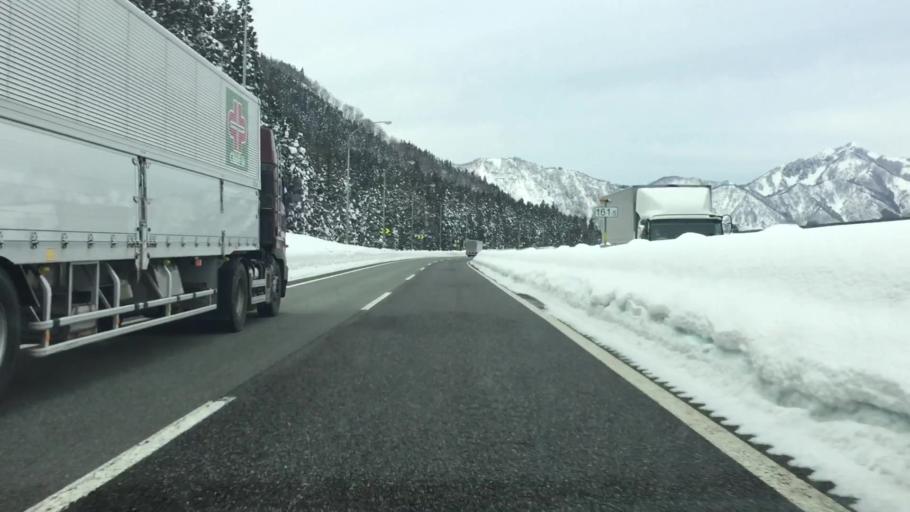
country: JP
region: Niigata
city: Shiozawa
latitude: 36.8916
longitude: 138.8470
